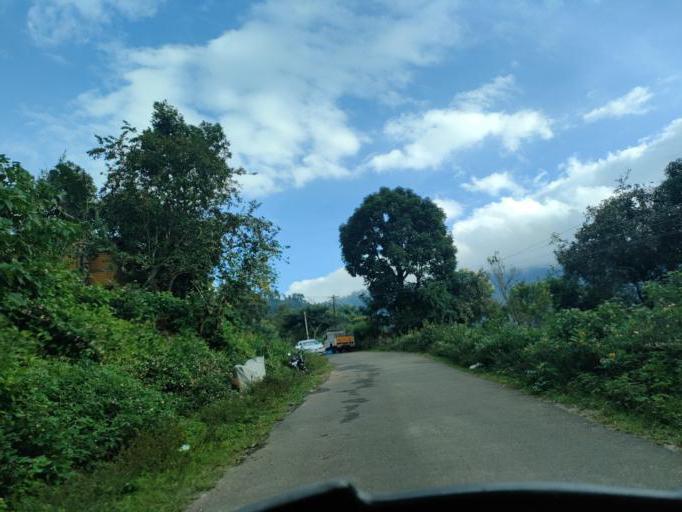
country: IN
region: Tamil Nadu
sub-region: Dindigul
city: Kodaikanal
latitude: 10.2786
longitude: 77.5311
